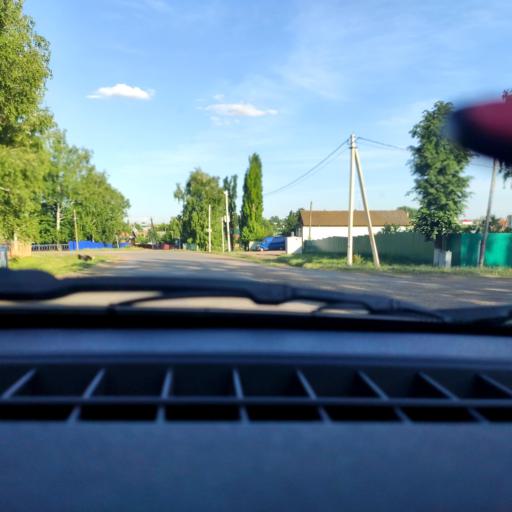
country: RU
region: Bashkortostan
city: Tolbazy
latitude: 54.2915
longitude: 55.8146
